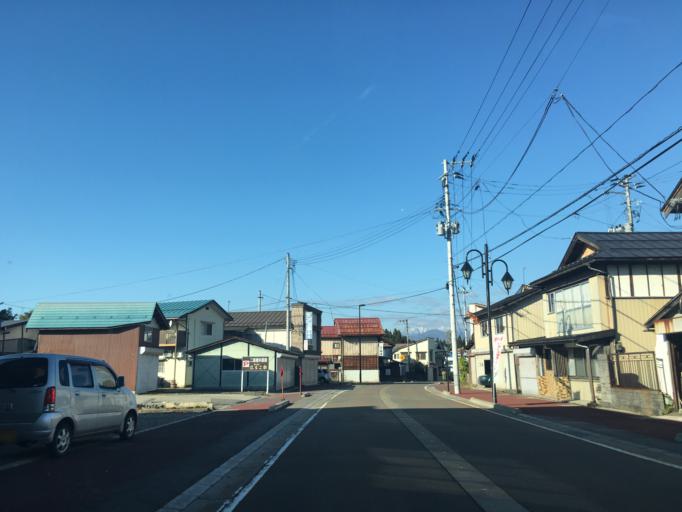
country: JP
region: Fukushima
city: Kitakata
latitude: 37.5886
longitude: 139.6449
